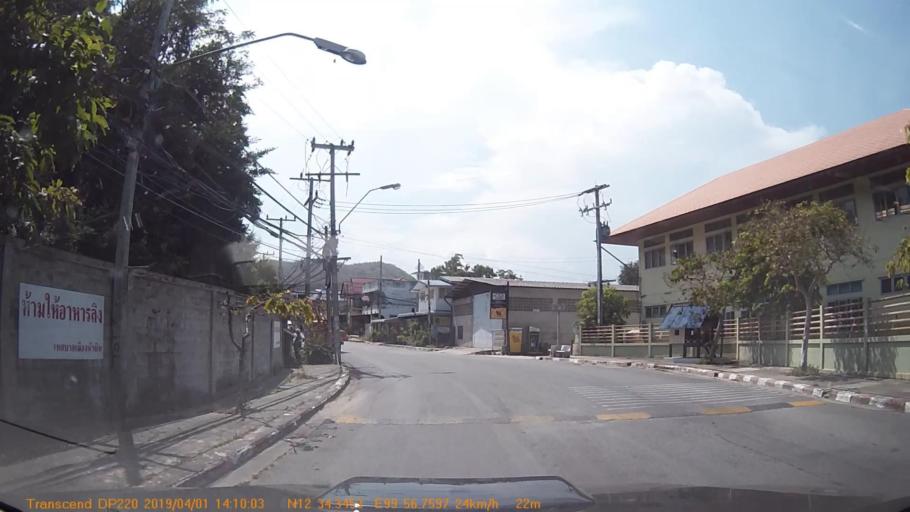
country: TH
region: Prachuap Khiri Khan
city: Hua Hin
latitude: 12.5726
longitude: 99.9458
